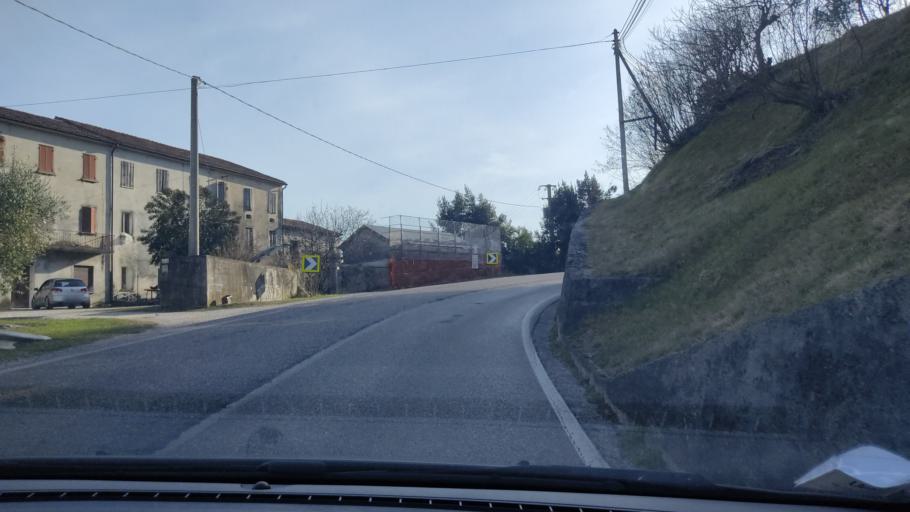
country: IT
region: Veneto
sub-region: Provincia di Treviso
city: Carpesica
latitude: 45.9574
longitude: 12.2831
